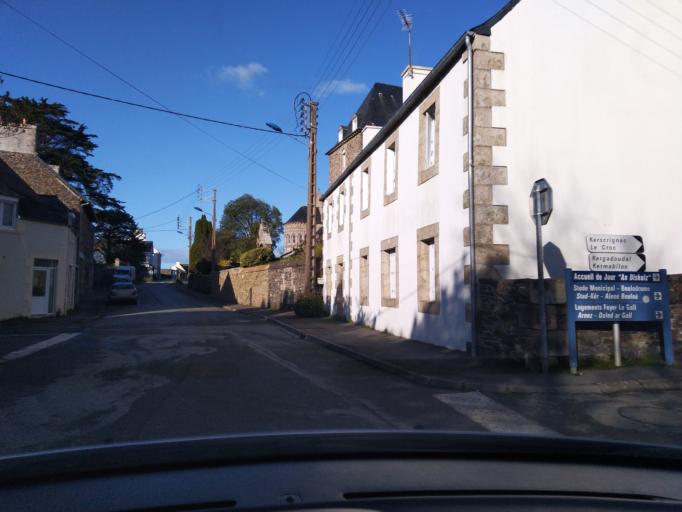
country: FR
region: Brittany
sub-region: Departement des Cotes-d'Armor
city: Plestin-les-Greves
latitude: 48.6577
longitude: -3.6306
